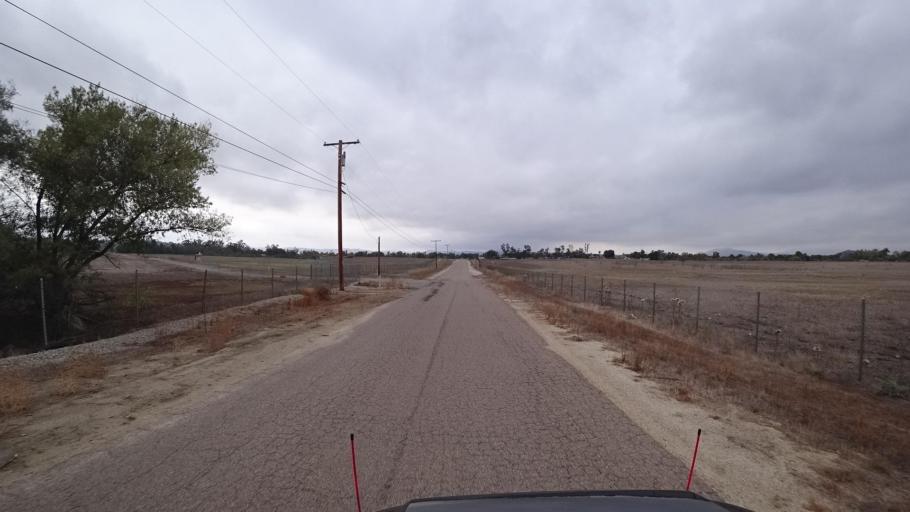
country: US
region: California
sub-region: San Diego County
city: Ramona
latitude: 33.0358
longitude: -116.9077
